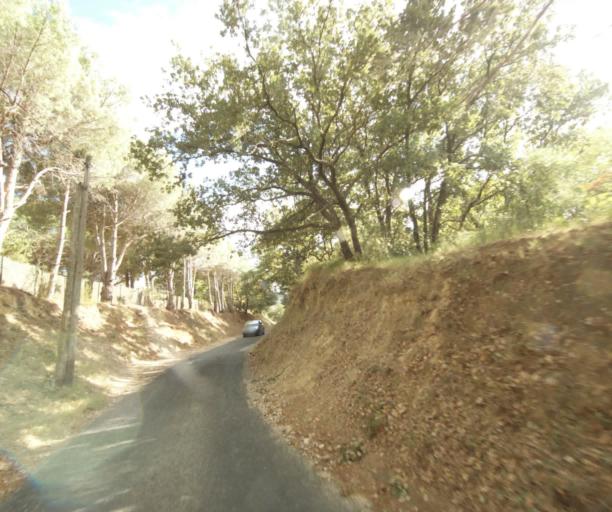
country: FR
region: Languedoc-Roussillon
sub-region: Departement des Pyrenees-Orientales
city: Argelers
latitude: 42.5372
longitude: 3.0252
